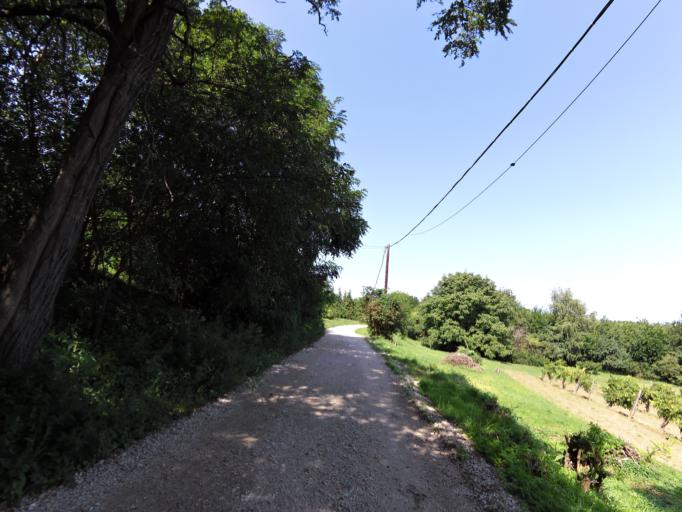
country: HU
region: Zala
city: Vonyarcvashegy
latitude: 46.8177
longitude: 17.3714
